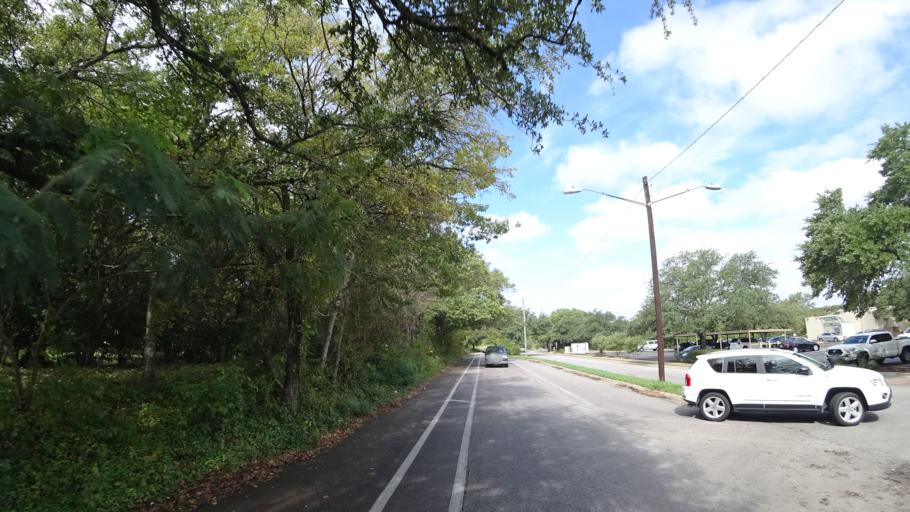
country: US
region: Texas
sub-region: Travis County
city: Austin
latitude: 30.3528
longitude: -97.7346
